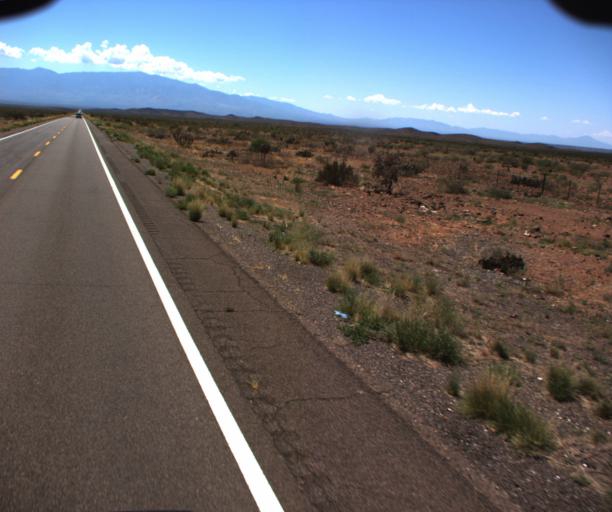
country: US
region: Arizona
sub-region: Graham County
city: Safford
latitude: 32.8267
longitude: -109.4609
